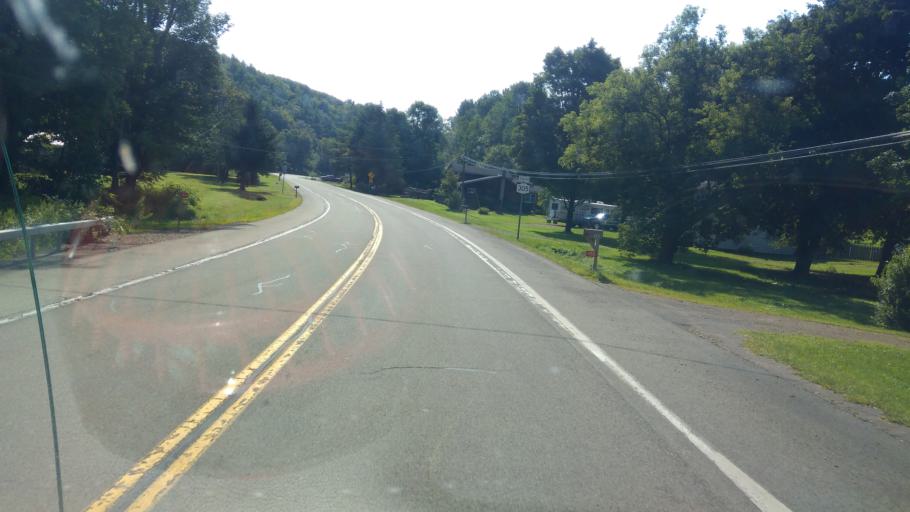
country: US
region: New York
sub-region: Allegany County
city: Cuba
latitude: 42.1968
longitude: -78.2709
